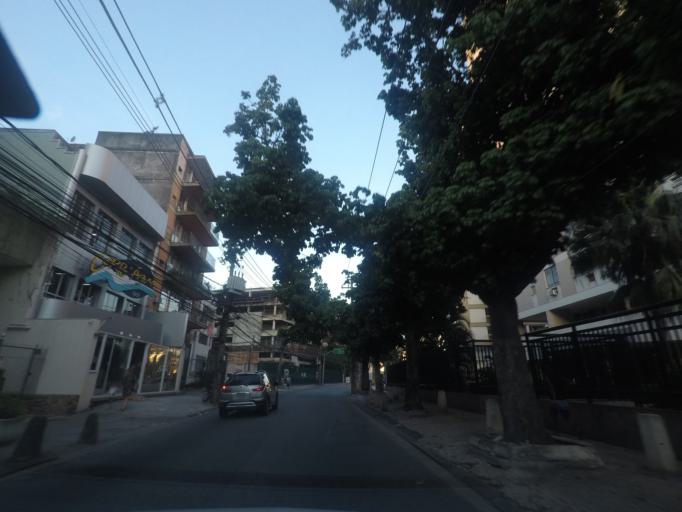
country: BR
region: Rio de Janeiro
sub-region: Rio De Janeiro
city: Rio de Janeiro
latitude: -22.9401
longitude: -43.3384
